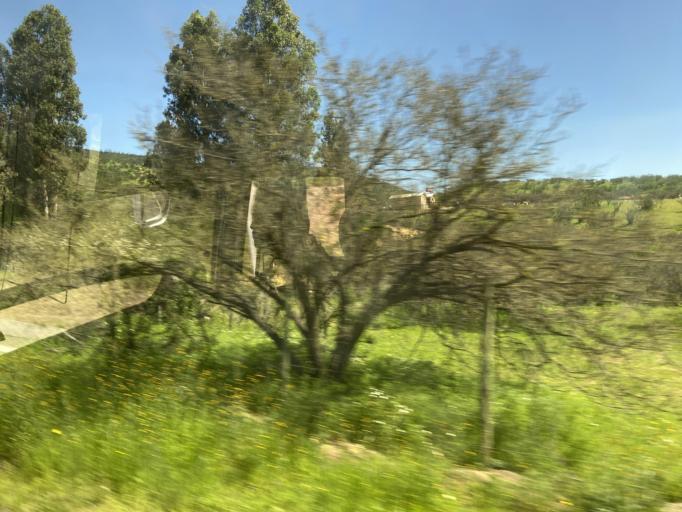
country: CL
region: Valparaiso
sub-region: Provincia de Marga Marga
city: Villa Alemana
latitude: -33.1704
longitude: -71.3133
